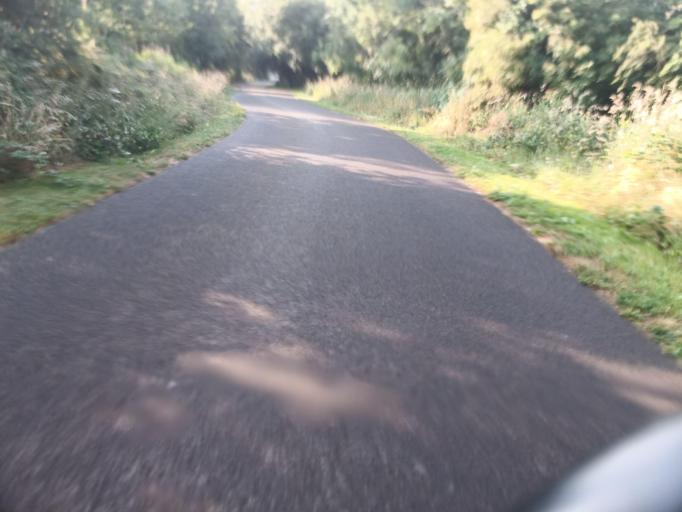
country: GB
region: Northern Ireland
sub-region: Castlereagh District
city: Dundonald
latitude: 54.5805
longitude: -5.7882
